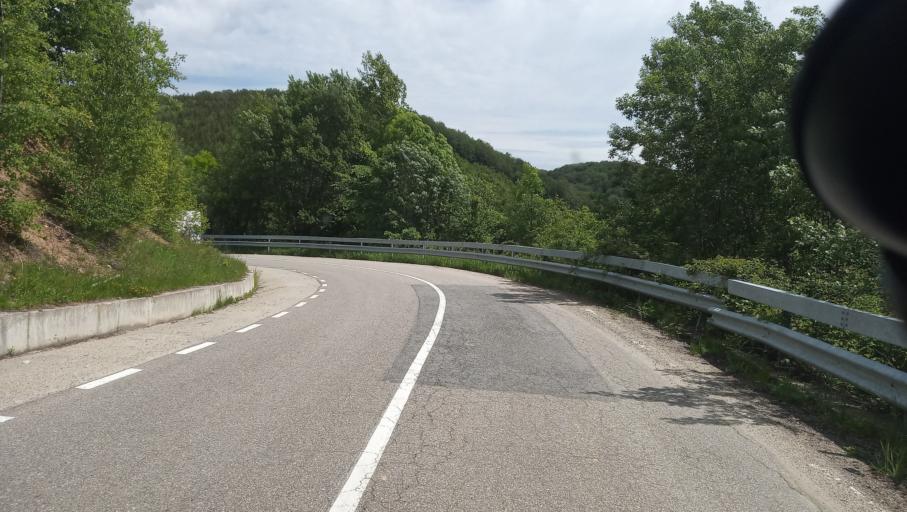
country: RO
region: Caras-Severin
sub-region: Comuna Brebu Nou
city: Brebu Nou
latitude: 45.2488
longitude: 22.1603
